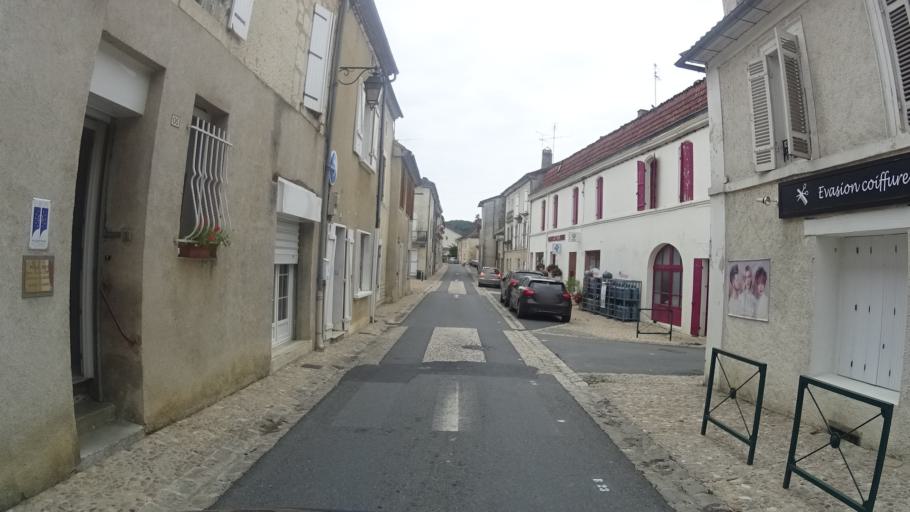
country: FR
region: Aquitaine
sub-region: Departement de la Dordogne
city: Neuvic
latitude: 45.0203
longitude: 0.5377
